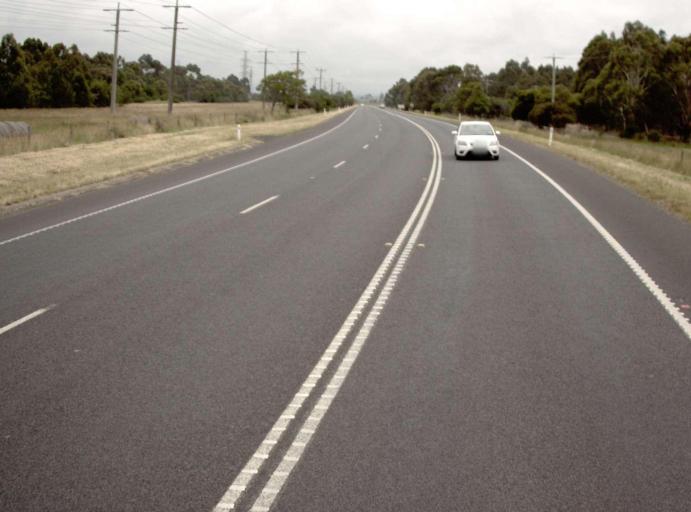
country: AU
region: Victoria
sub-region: Latrobe
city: Morwell
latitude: -38.2762
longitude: 146.4203
